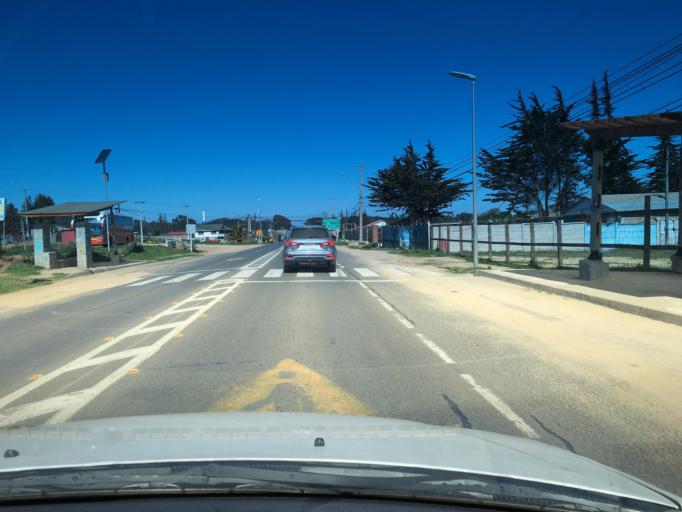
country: CL
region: Valparaiso
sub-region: San Antonio Province
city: El Tabo
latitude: -33.4321
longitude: -71.6877
